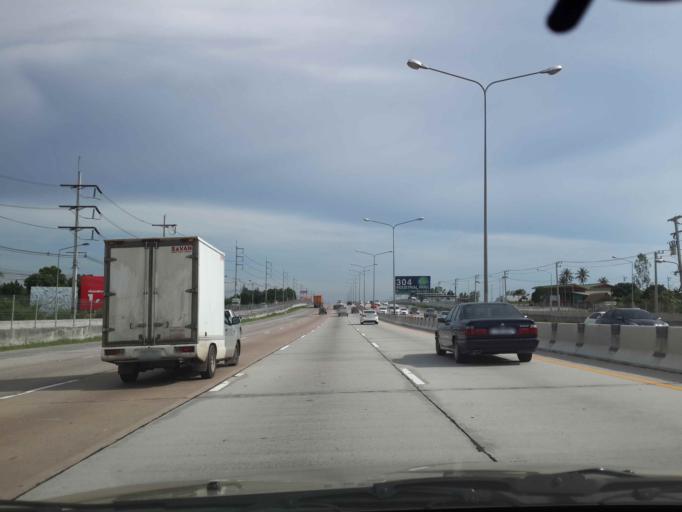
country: TH
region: Chon Buri
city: Si Racha
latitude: 13.1716
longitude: 100.9924
